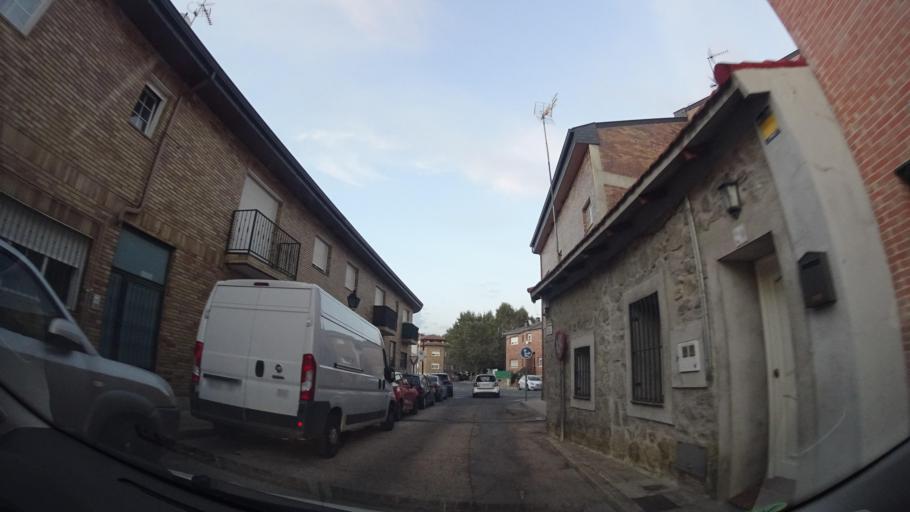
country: ES
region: Madrid
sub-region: Provincia de Madrid
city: Colmenarejo
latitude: 40.5625
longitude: -4.0176
